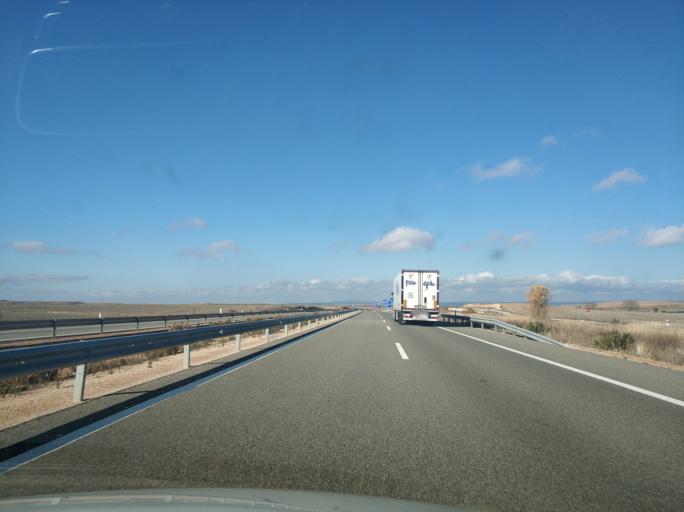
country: ES
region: Castille and Leon
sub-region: Provincia de Soria
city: Coscurita
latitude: 41.4052
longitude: -2.4802
